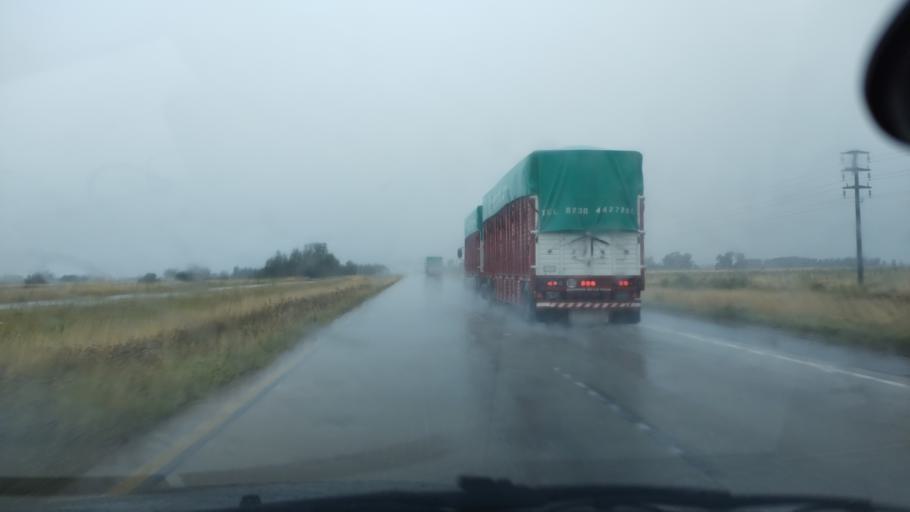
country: AR
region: Buenos Aires
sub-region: Partido de San Vicente
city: San Vicente
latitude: -35.0699
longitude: -58.5213
